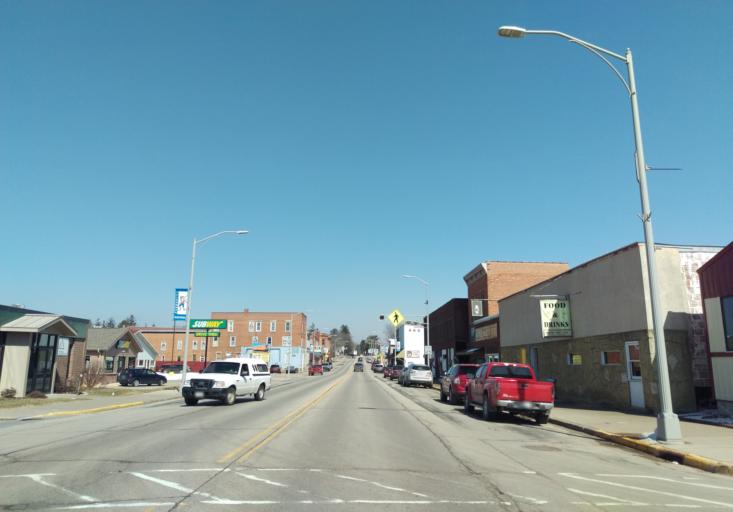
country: US
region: Wisconsin
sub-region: Vernon County
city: Westby
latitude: 43.6519
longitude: -90.8583
